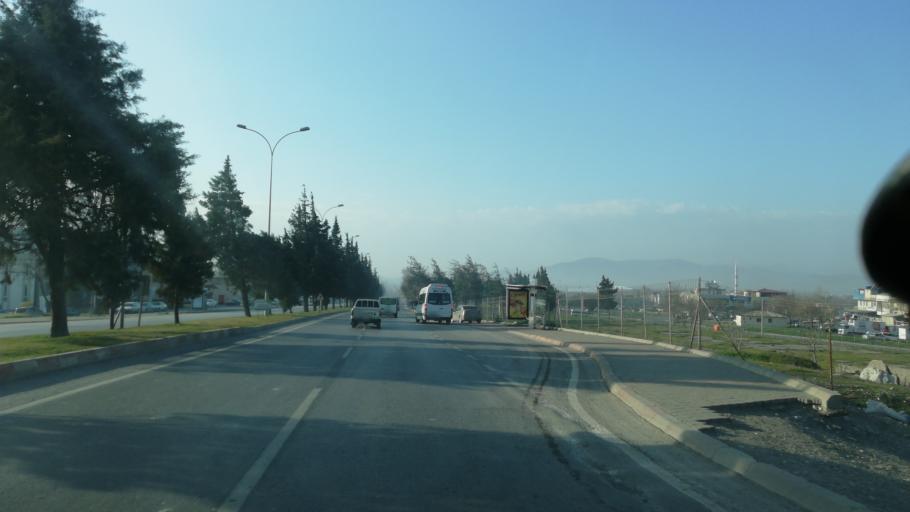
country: TR
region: Kahramanmaras
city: Kahramanmaras
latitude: 37.5659
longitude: 36.9242
